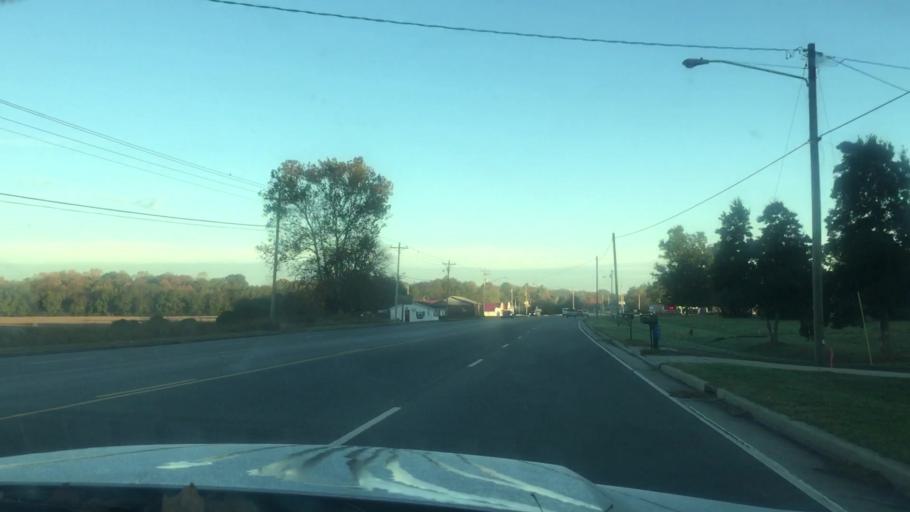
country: US
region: Tennessee
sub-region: Franklin County
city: Estill Springs
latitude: 35.2528
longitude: -86.1207
